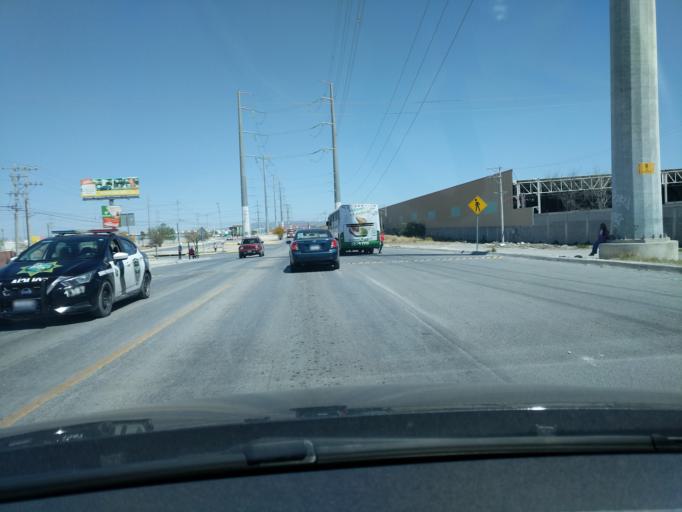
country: MX
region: Nuevo Leon
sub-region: Apodaca
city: Artemio Trevino
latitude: 25.8380
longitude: -100.1377
